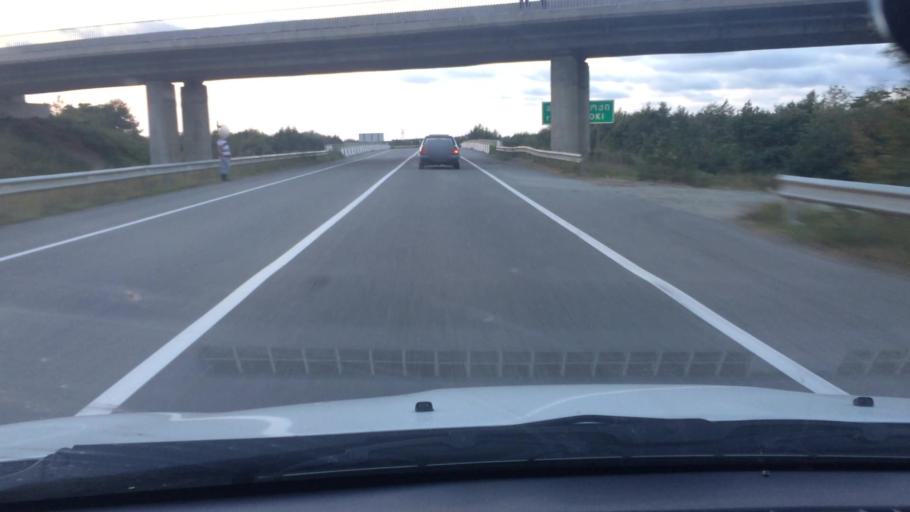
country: GE
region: Ajaria
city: Ochkhamuri
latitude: 41.8922
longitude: 41.8052
